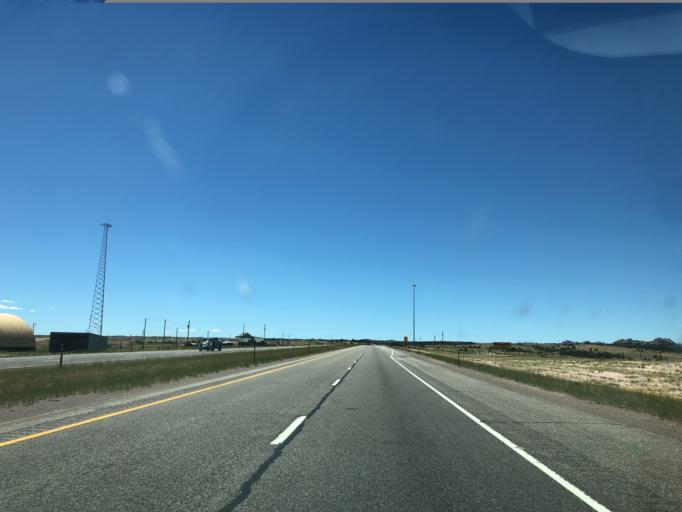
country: US
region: Wyoming
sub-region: Albany County
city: Laramie
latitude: 41.1241
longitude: -105.2974
